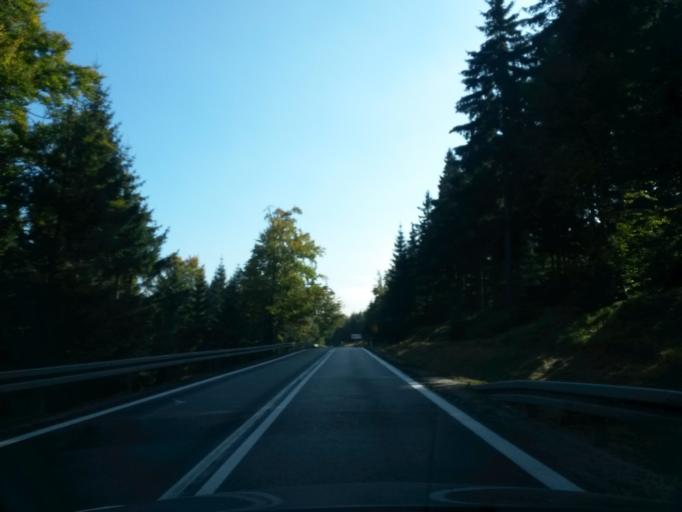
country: CZ
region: Liberecky
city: Harrachov
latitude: 50.8262
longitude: 15.4587
